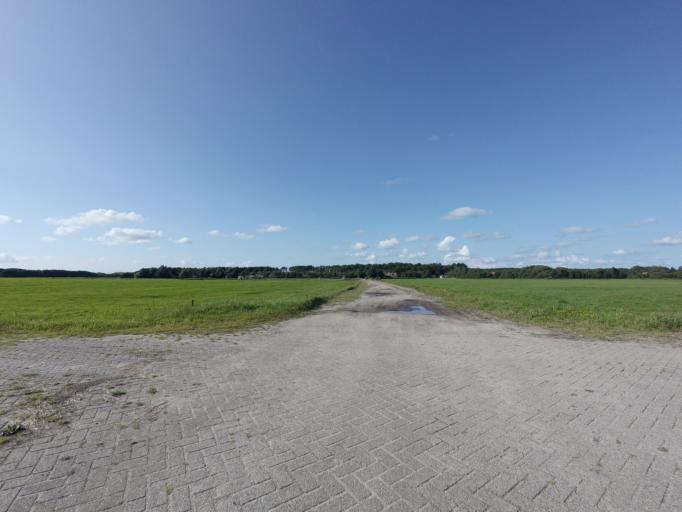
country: NL
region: Friesland
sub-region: Gemeente Terschelling
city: West-Terschelling
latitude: 53.3857
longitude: 5.2733
